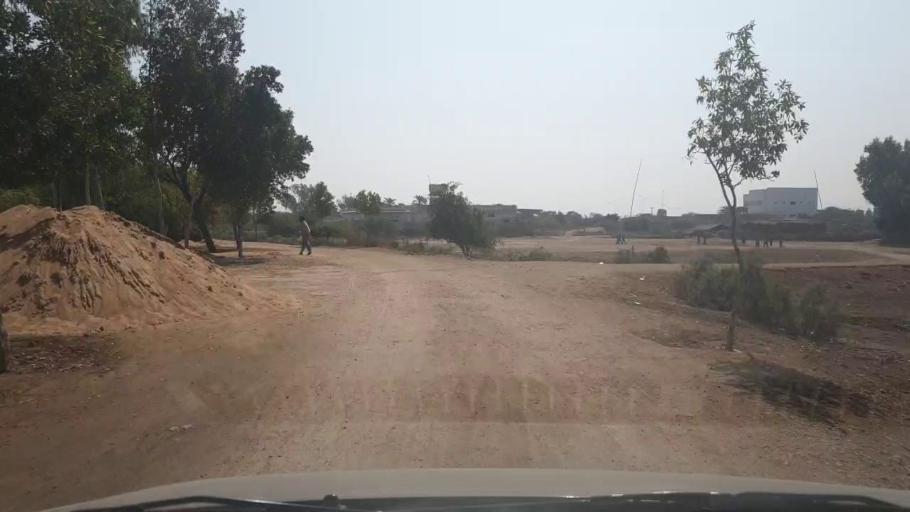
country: PK
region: Sindh
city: Mirwah Gorchani
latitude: 25.2766
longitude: 69.1351
